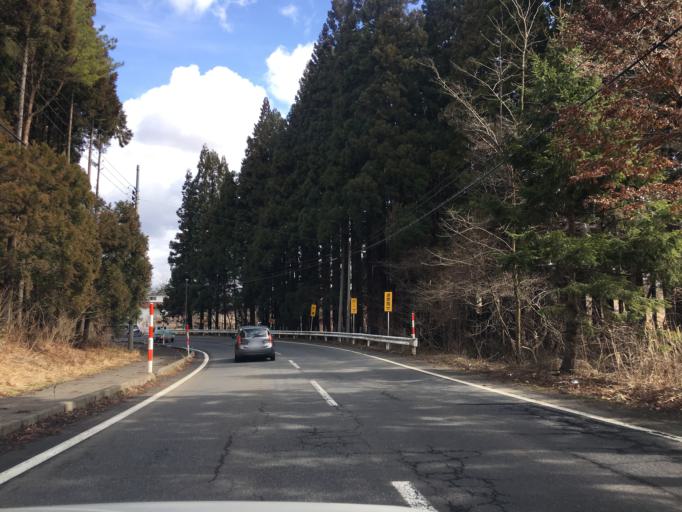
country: JP
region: Akita
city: Odate
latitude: 40.2020
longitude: 140.5541
